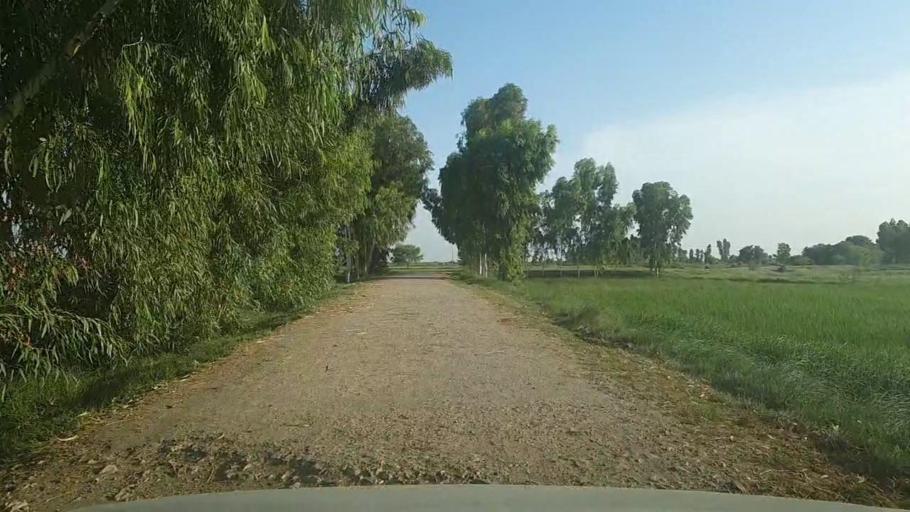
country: PK
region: Sindh
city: Khairpur
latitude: 28.0863
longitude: 69.6387
